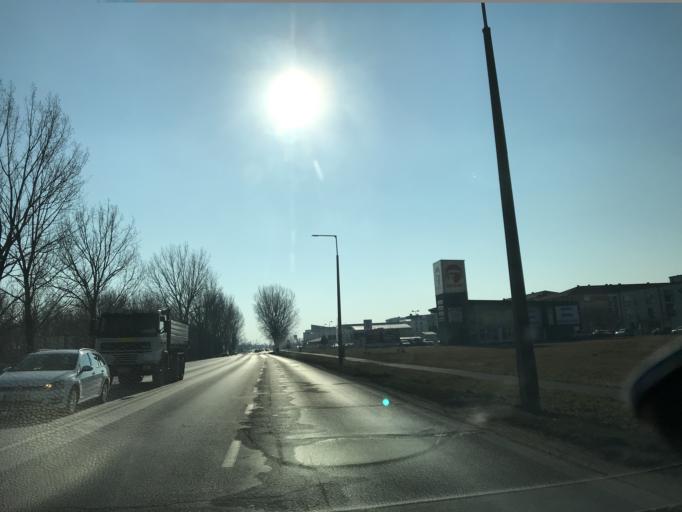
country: HU
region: Gyor-Moson-Sopron
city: Gyor
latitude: 47.6603
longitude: 17.6375
